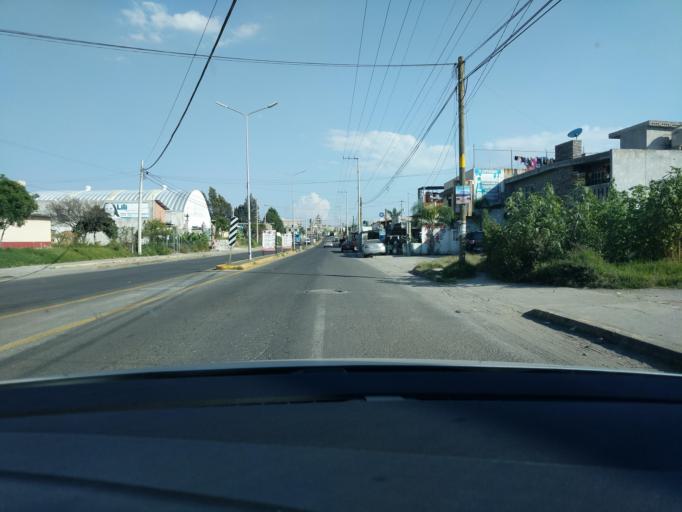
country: MX
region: Puebla
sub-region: San Gregorio Atzompa
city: Chipilo de Francisco Javier Mina
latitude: 19.0255
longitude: -98.3135
